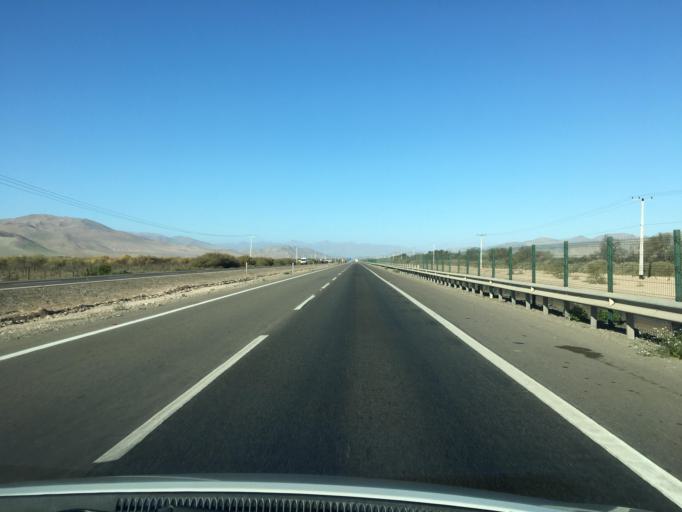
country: CL
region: Atacama
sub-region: Provincia de Copiapo
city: Copiapo
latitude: -27.3367
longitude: -70.5923
